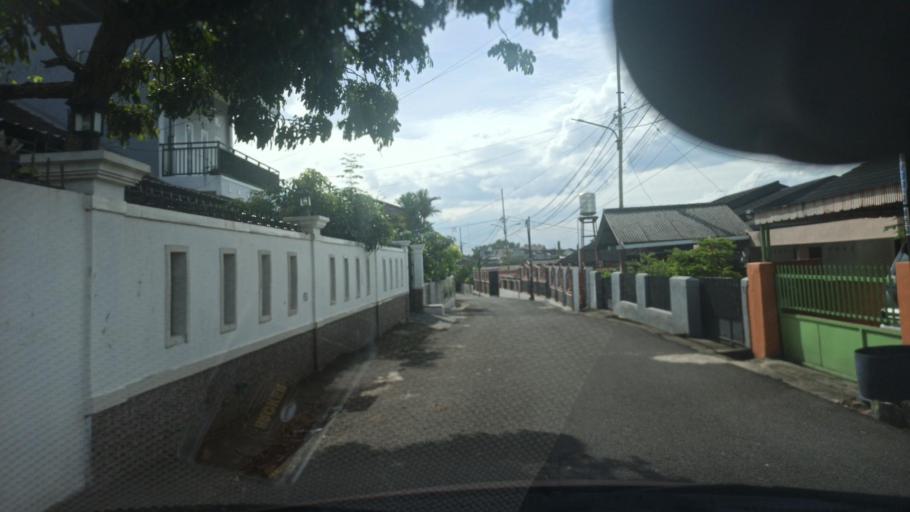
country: ID
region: South Sumatra
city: Plaju
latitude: -2.9923
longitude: 104.7231
